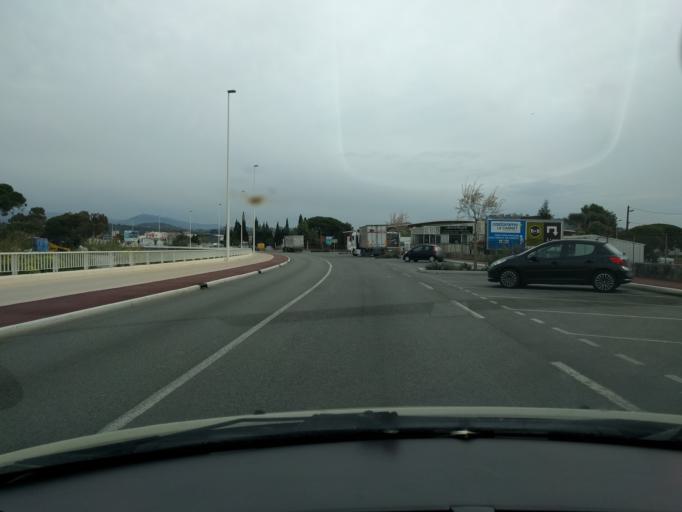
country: FR
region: Provence-Alpes-Cote d'Azur
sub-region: Departement des Alpes-Maritimes
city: Mandelieu-la-Napoule
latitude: 43.5450
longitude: 6.9615
